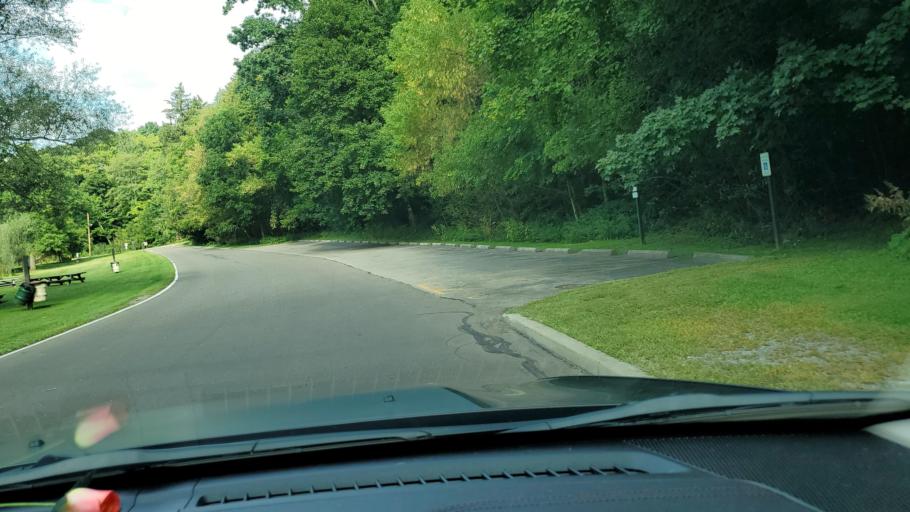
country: US
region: Ohio
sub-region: Mahoning County
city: Youngstown
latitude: 41.0978
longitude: -80.6790
